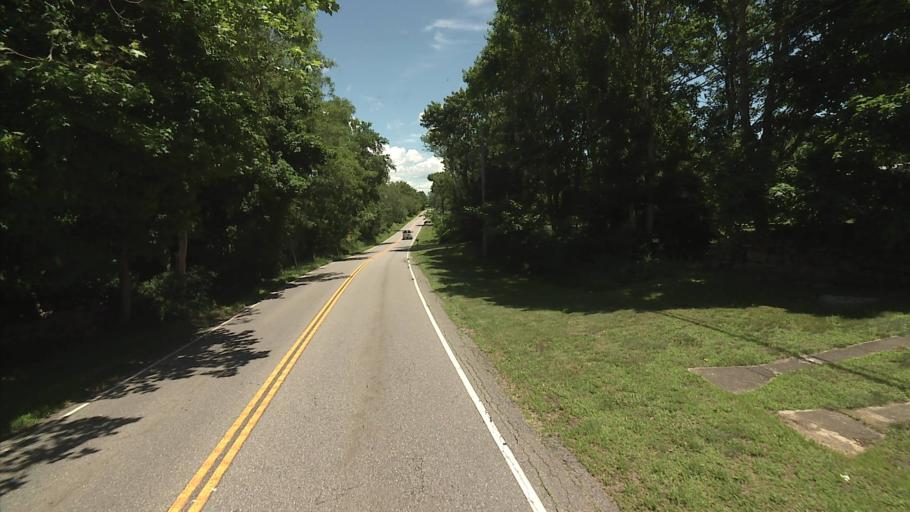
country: US
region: Connecticut
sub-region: New London County
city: Pawcatuck
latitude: 41.3800
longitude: -71.8981
